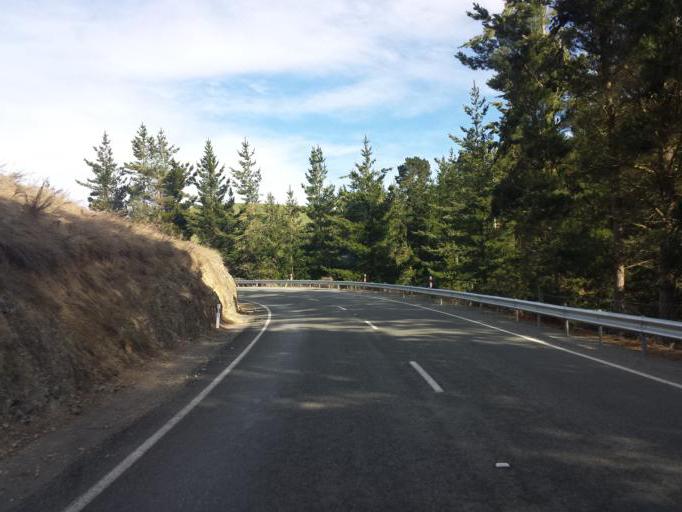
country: NZ
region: Canterbury
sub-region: Timaru District
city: Pleasant Point
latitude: -44.0496
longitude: 170.8967
